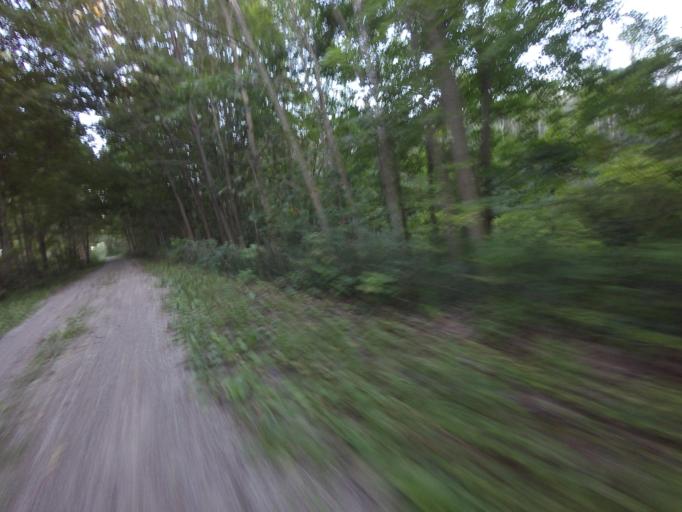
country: CA
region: Ontario
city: Goderich
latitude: 43.7470
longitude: -81.6399
